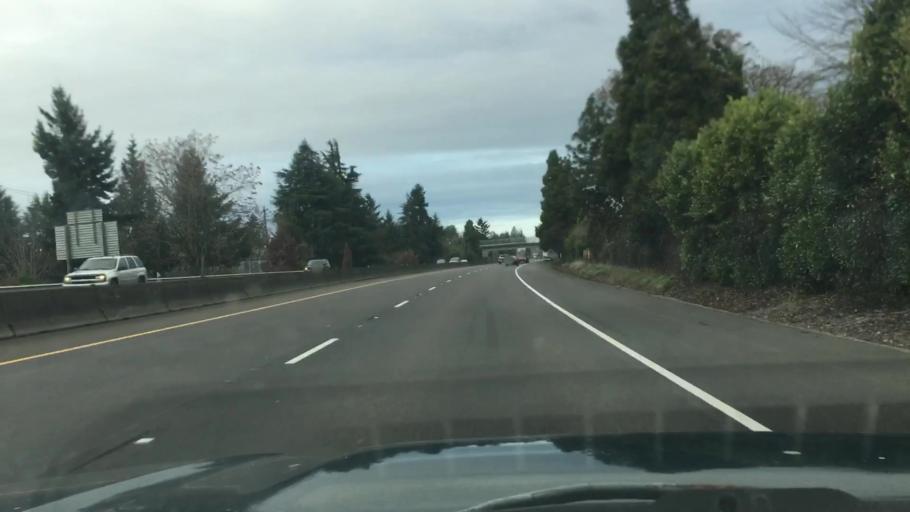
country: US
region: Oregon
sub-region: Lane County
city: Eugene
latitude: 44.0883
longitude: -123.0833
